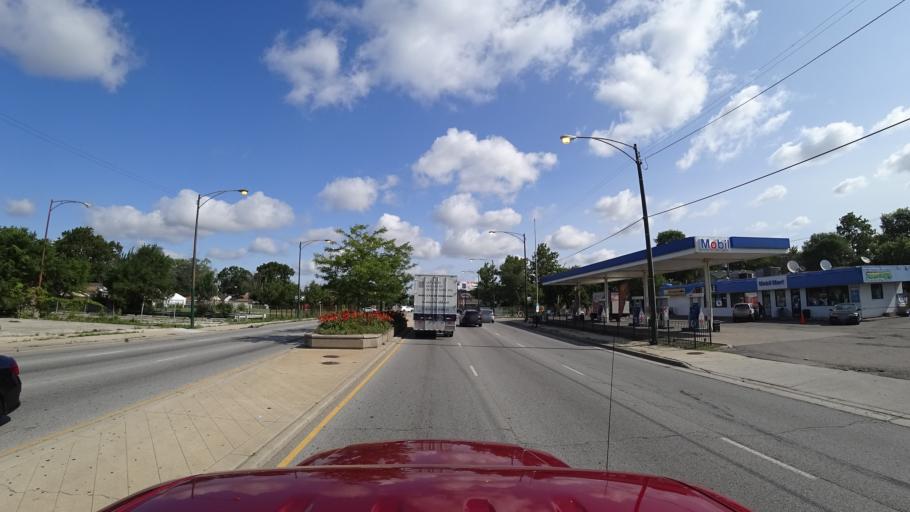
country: US
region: Illinois
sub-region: Cook County
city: Cicero
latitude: 41.8085
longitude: -87.7431
